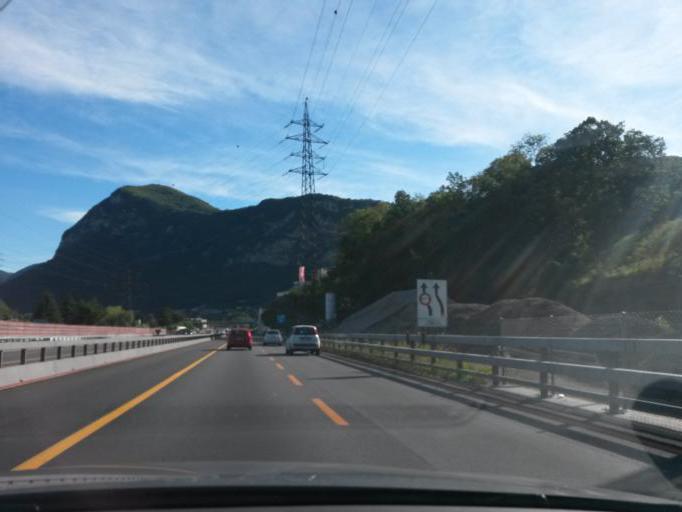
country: CH
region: Ticino
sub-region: Mendrisio District
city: Mendrisio
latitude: 45.8698
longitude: 8.9731
